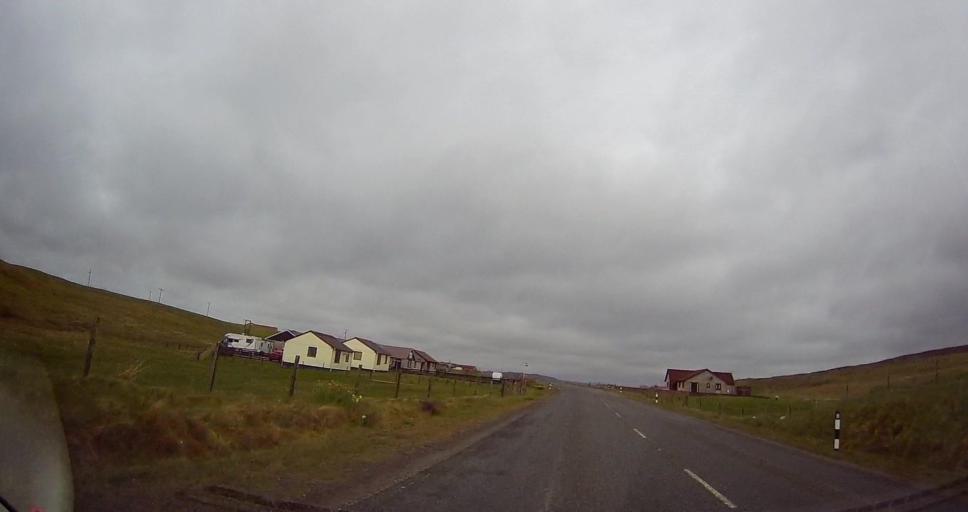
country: GB
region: Scotland
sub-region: Shetland Islands
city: Lerwick
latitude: 60.3765
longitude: -1.3390
